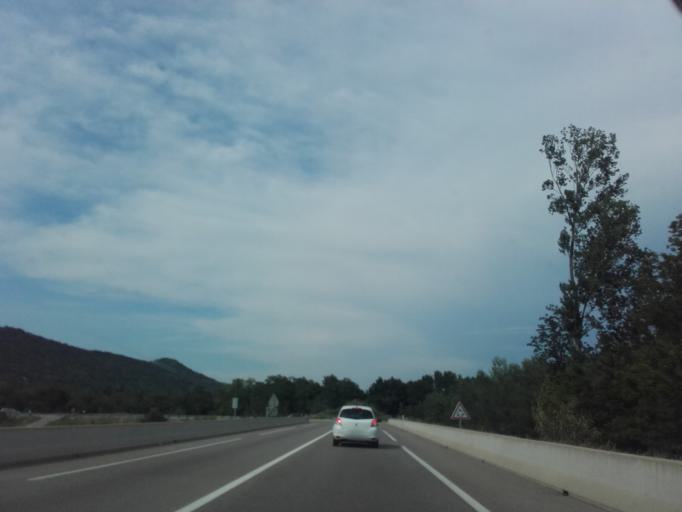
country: FR
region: Rhone-Alpes
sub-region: Departement de l'Ardeche
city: Rochemaure
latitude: 44.5791
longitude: 4.7026
